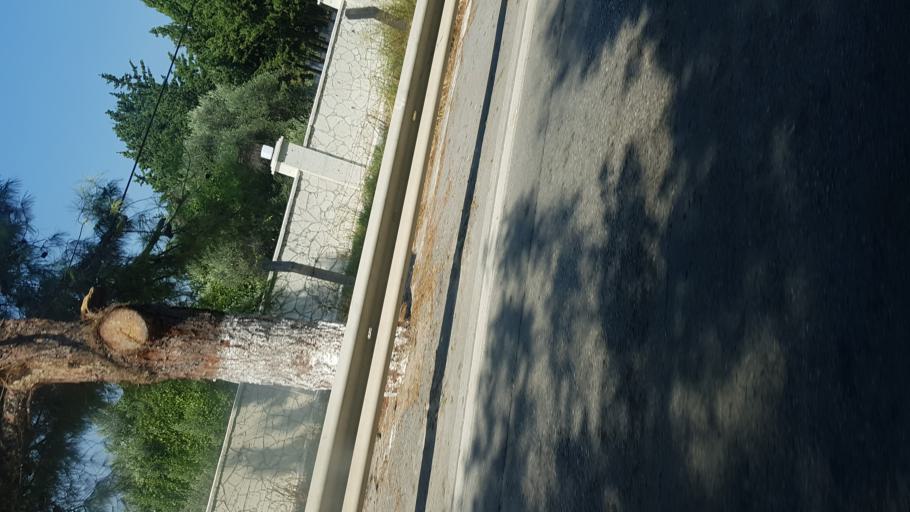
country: TR
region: Izmir
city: Urla
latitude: 38.3480
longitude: 26.7717
